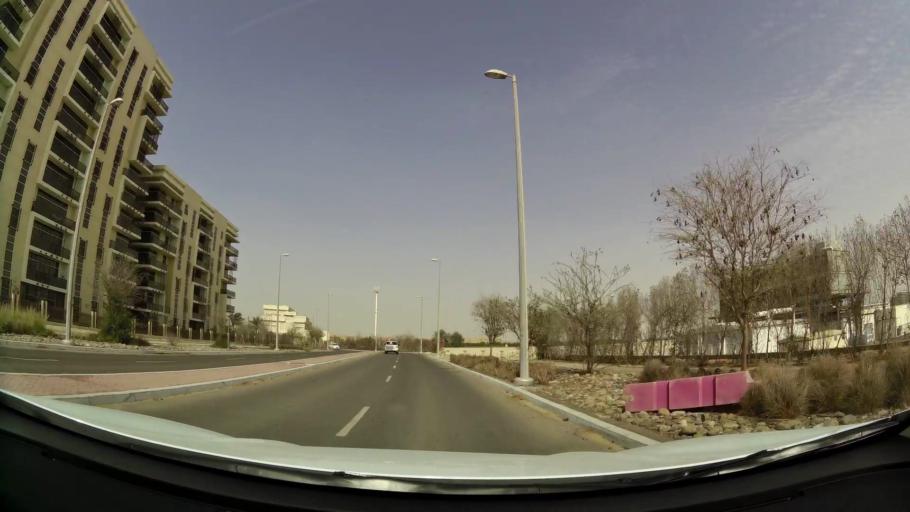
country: AE
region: Abu Dhabi
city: Abu Dhabi
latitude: 24.4092
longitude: 54.5374
